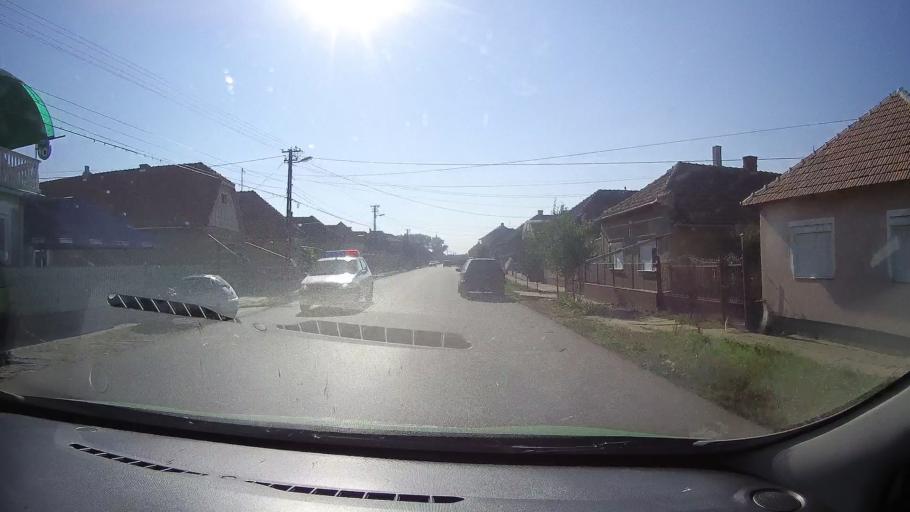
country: RO
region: Satu Mare
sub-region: Comuna Camin
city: Camin
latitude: 47.7332
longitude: 22.4768
